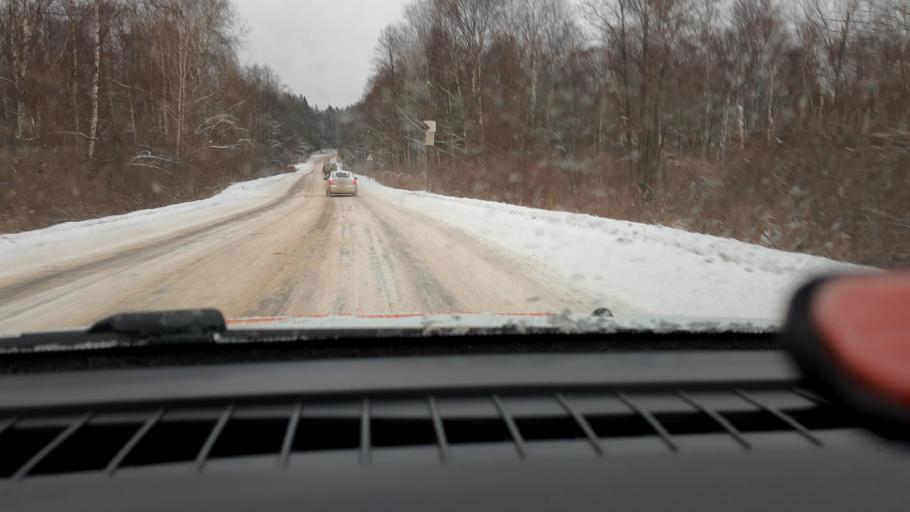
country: RU
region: Nizjnij Novgorod
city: Kstovo
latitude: 56.2791
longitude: 44.3664
